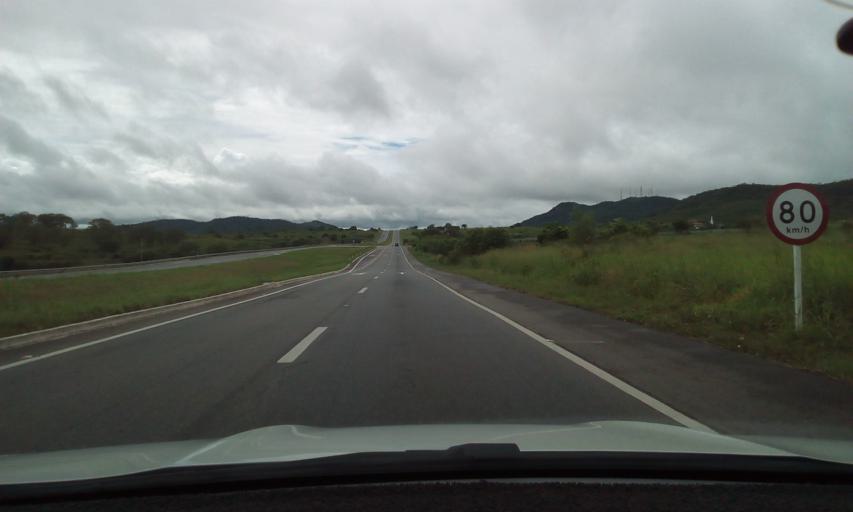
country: BR
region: Paraiba
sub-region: Gurinhem
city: Gurinhem
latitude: -7.1858
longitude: -35.4491
